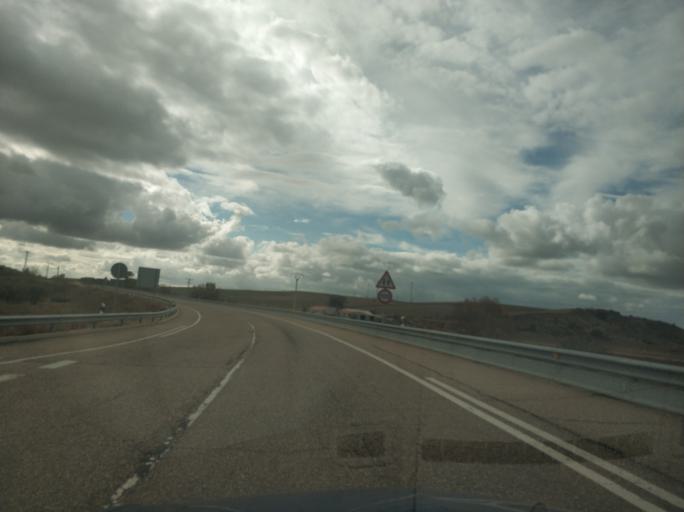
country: ES
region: Castille and Leon
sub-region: Provincia de Valladolid
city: Torrecilla de la Abadesa
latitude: 41.4535
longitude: -5.0885
